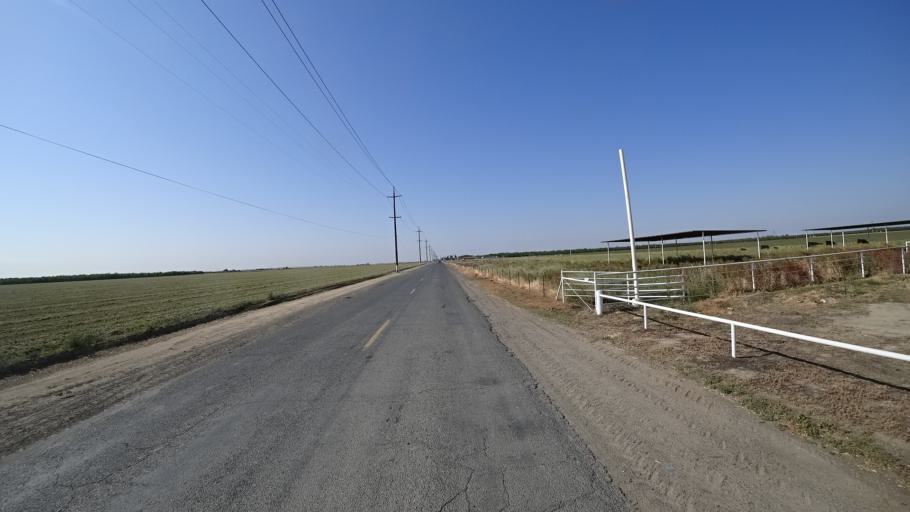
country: US
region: California
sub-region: Kings County
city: Home Garden
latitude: 36.2678
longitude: -119.5831
